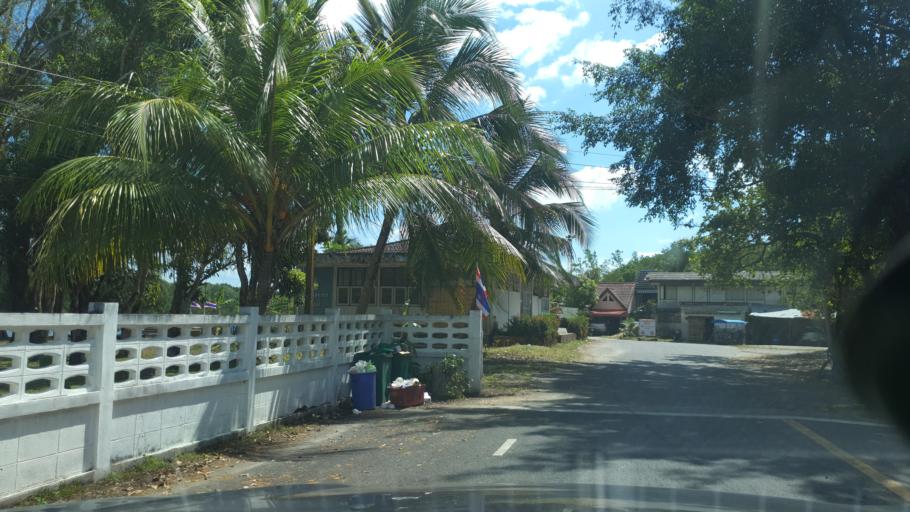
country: TH
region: Phangnga
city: Phang Nga
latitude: 8.3968
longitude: 98.5142
